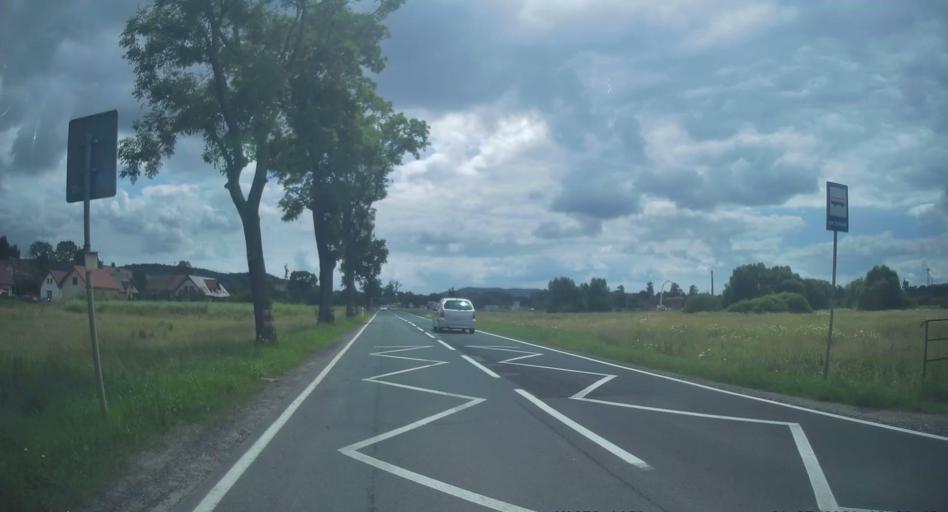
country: PL
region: Lower Silesian Voivodeship
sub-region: Powiat kamiennogorski
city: Kamienna Gora
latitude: 50.7997
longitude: 16.0388
